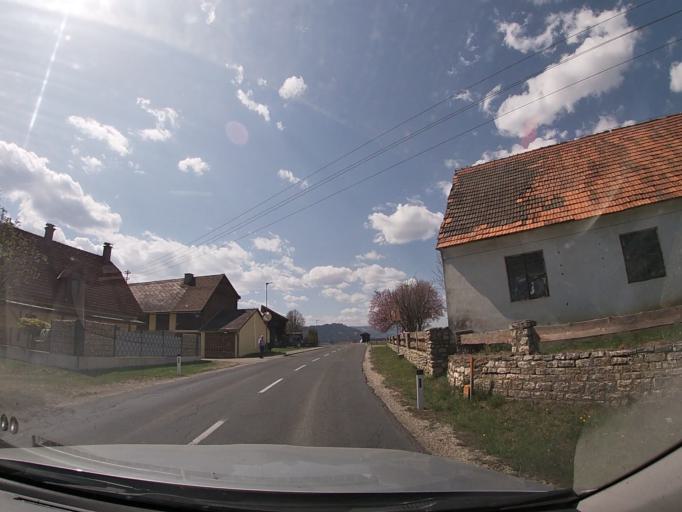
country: AT
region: Styria
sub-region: Politischer Bezirk Murtal
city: Zeltweg
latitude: 47.1701
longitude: 14.7513
